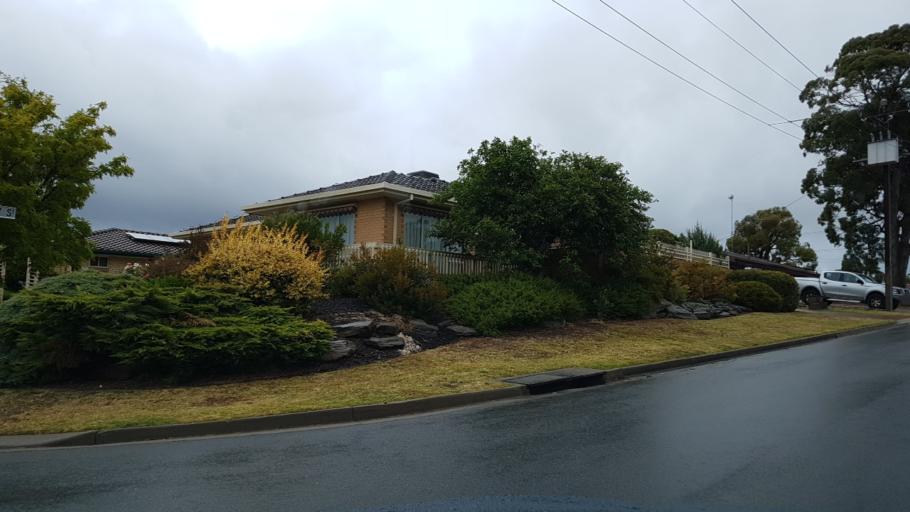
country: AU
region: South Australia
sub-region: Onkaparinga
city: Bedford Park
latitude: -35.0425
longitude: 138.5721
